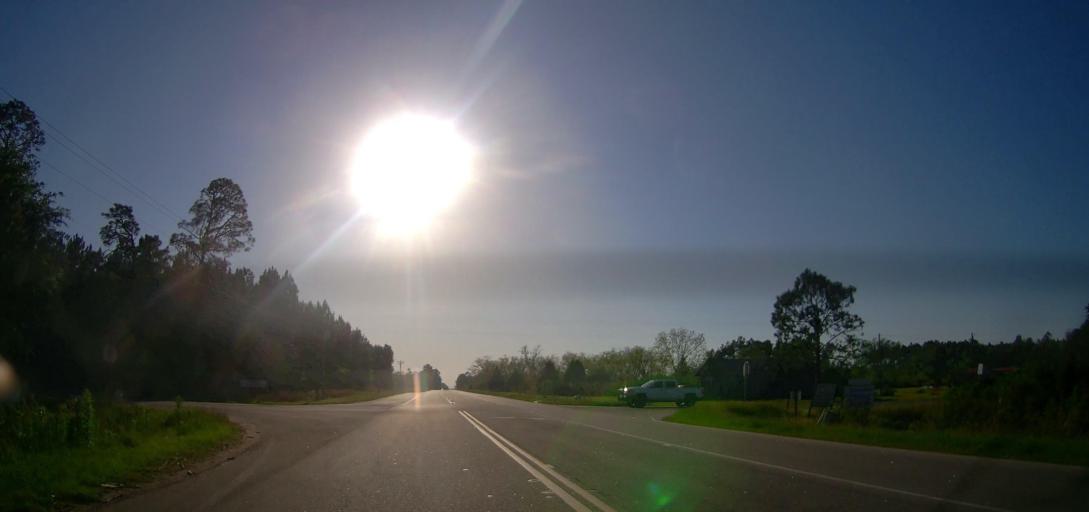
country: US
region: Georgia
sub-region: Ben Hill County
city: Fitzgerald
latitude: 31.7132
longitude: -83.2047
